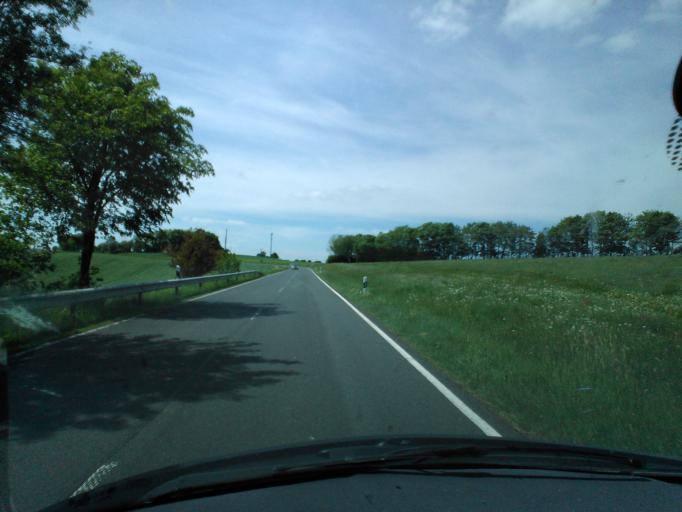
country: DE
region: Rheinland-Pfalz
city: Kickeshausen
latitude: 50.0790
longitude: 6.2433
